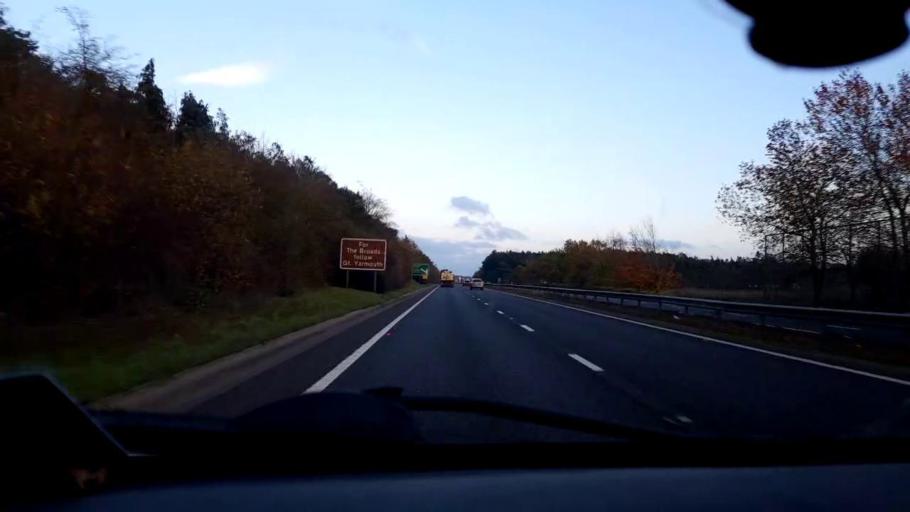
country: GB
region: England
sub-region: Norfolk
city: Costessey
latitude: 52.6545
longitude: 1.1654
